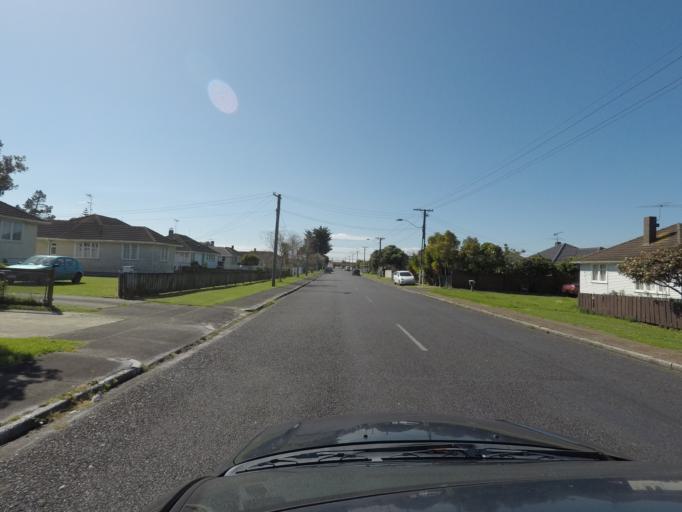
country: NZ
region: Auckland
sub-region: Auckland
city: Tamaki
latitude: -36.9283
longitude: 174.8560
